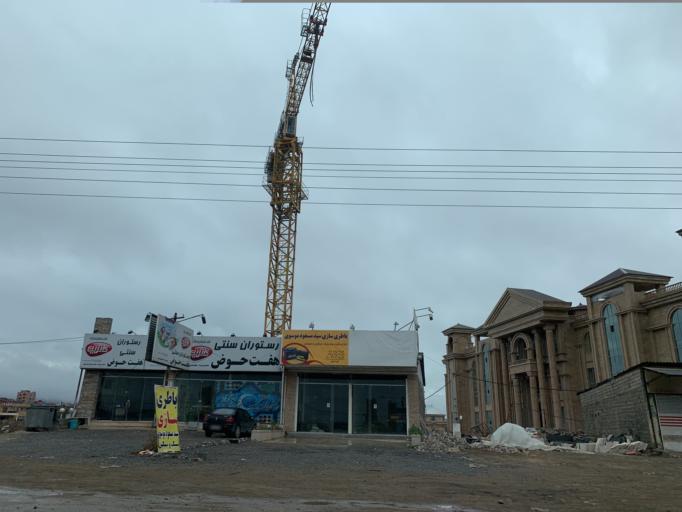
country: IR
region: Mazandaran
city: Amol
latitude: 36.4120
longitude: 52.3483
